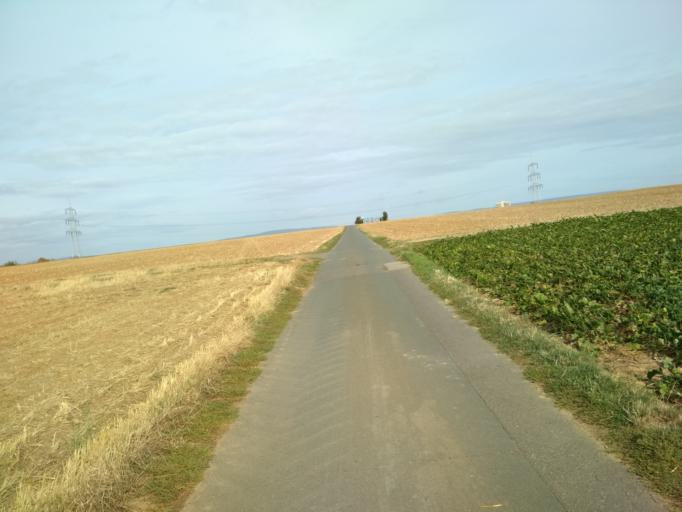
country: DE
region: Rheinland-Pfalz
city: Mainz
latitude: 49.9608
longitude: 8.2461
